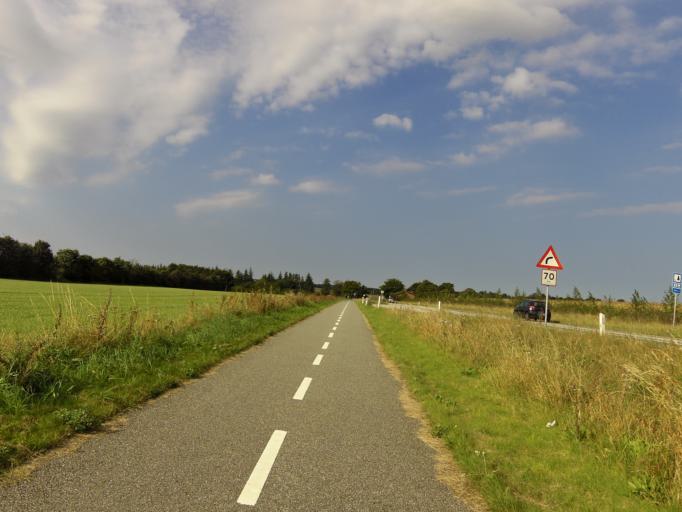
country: DK
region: South Denmark
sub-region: Vejen Kommune
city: Vejen
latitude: 55.4399
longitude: 9.1381
